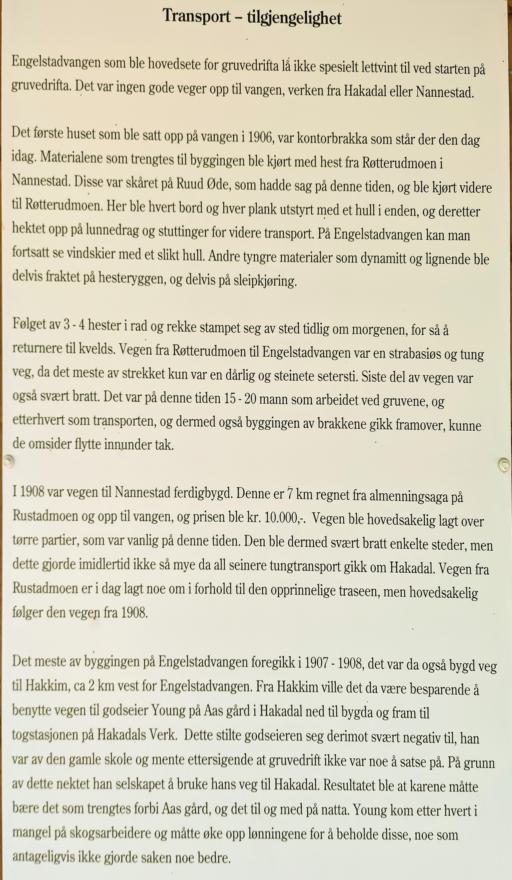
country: NO
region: Akershus
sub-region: Nittedal
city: Aneby
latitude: 60.1838
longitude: 10.8960
